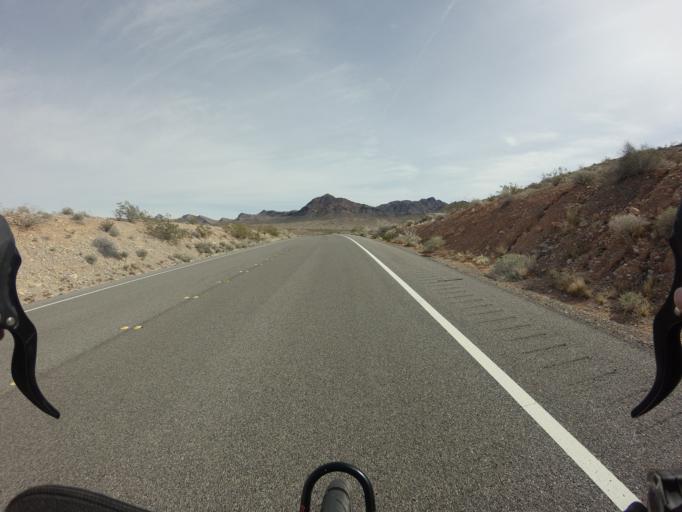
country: US
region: Nevada
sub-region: Clark County
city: Boulder City
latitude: 36.1963
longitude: -114.6919
